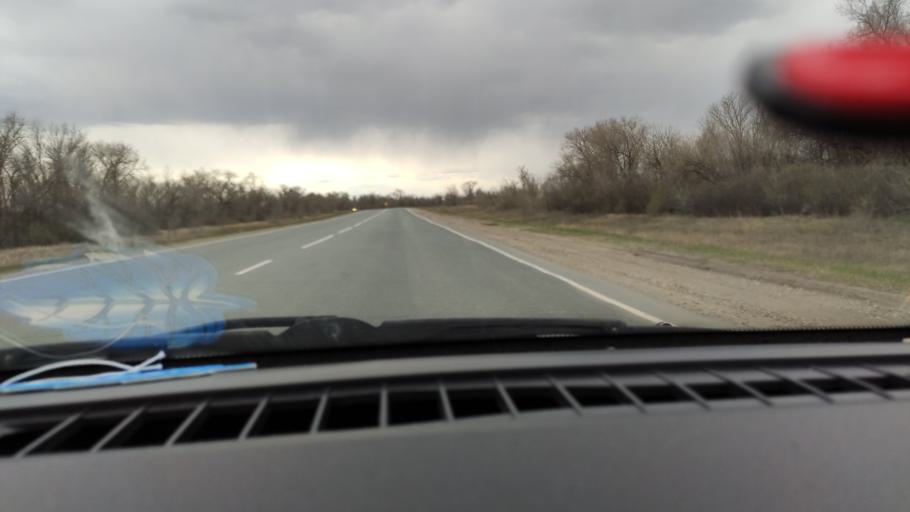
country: RU
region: Saratov
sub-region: Saratovskiy Rayon
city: Saratov
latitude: 51.7071
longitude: 46.0148
